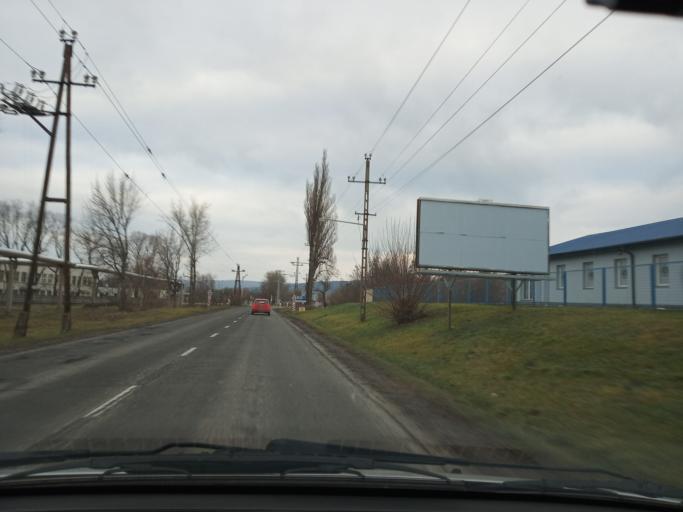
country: HU
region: Komarom-Esztergom
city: Dorog
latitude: 47.7522
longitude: 18.7323
